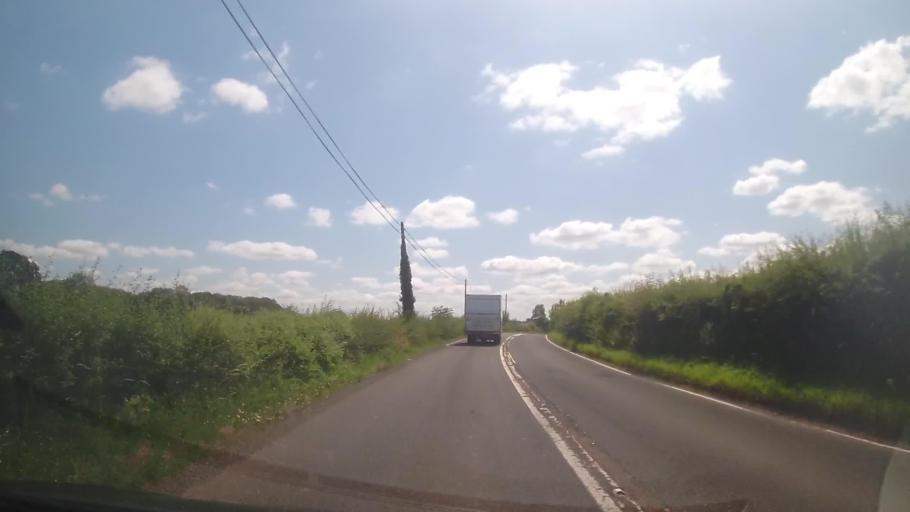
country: GB
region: England
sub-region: Herefordshire
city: Ocle Pychard
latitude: 52.1344
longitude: -2.6043
